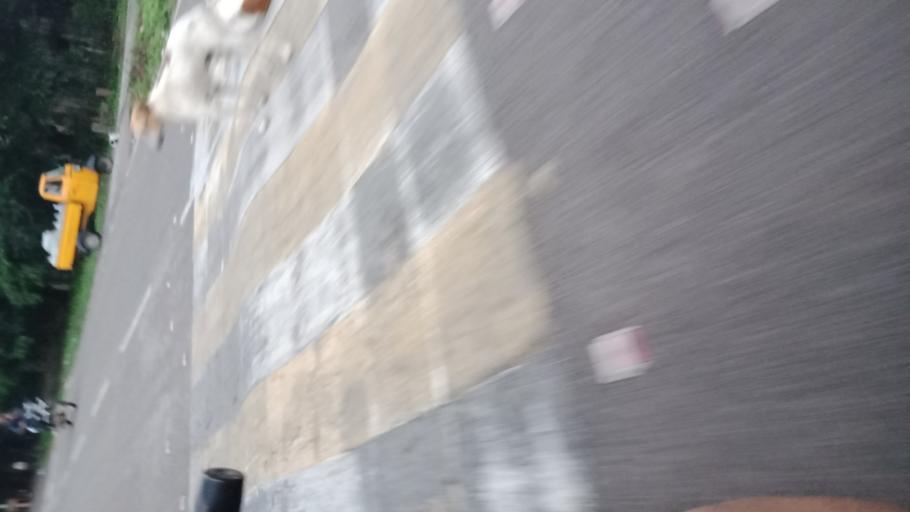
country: IN
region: Telangana
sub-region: Medak
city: Serilingampalle
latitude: 17.4981
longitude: 78.3084
